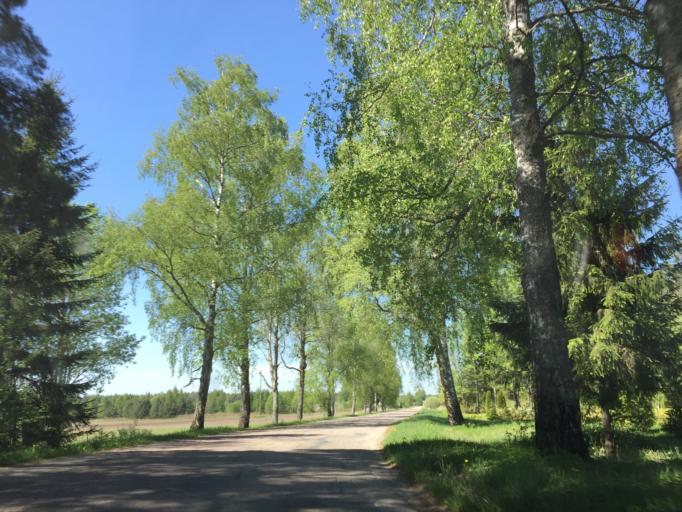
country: LV
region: Kegums
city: Kegums
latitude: 56.8518
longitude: 24.7182
